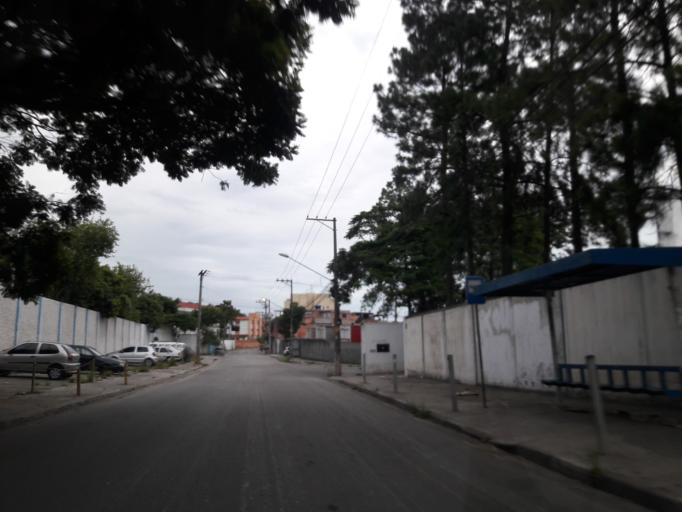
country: BR
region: Sao Paulo
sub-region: Aruja
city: Aruja
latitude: -23.4212
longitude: -46.3959
